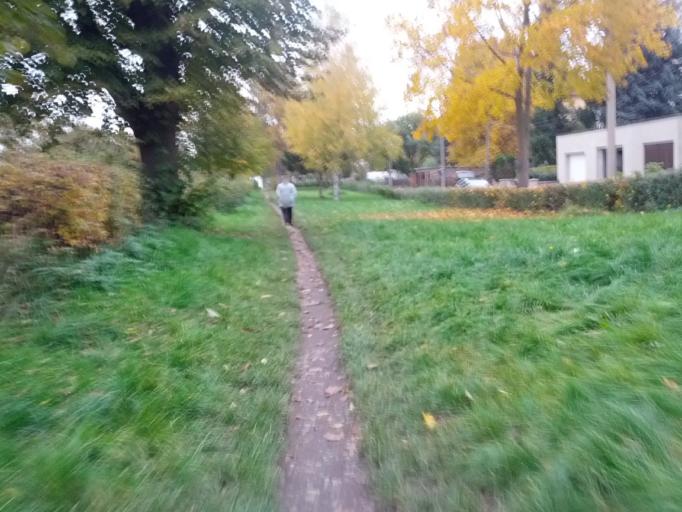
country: DE
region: Thuringia
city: Eisenach
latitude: 50.9738
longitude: 10.3451
